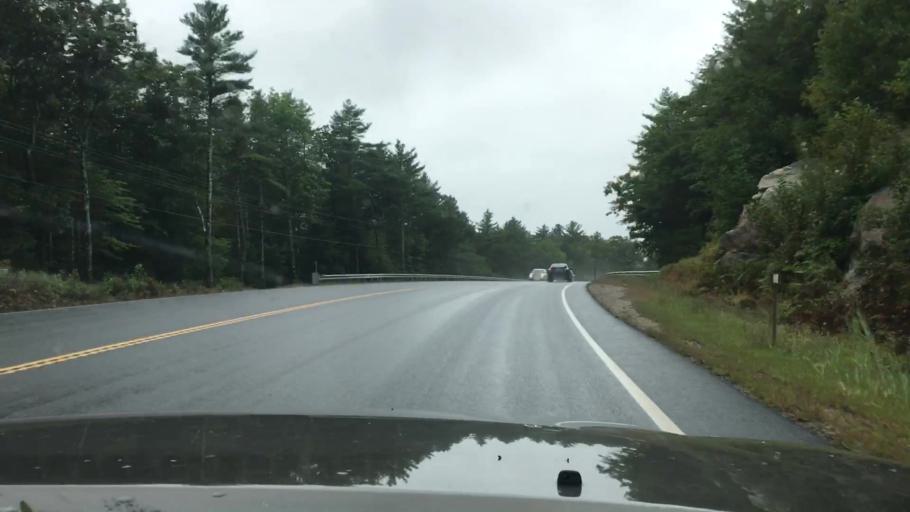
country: US
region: New Hampshire
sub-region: Cheshire County
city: Keene
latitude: 42.9678
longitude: -72.2479
